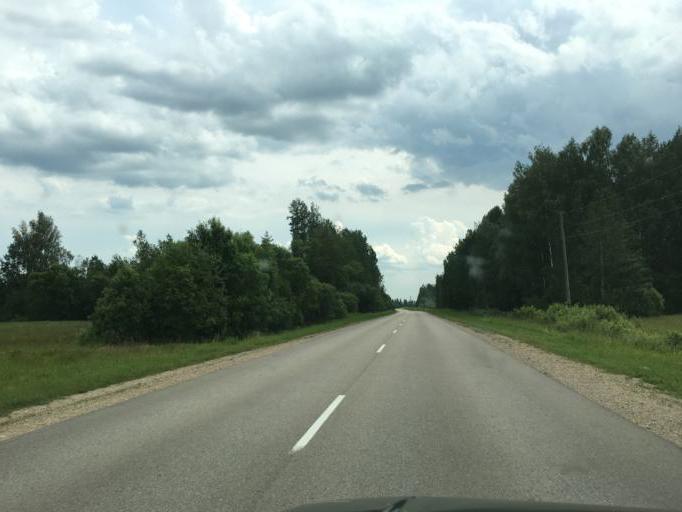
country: LV
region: Rugaju
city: Rugaji
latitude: 56.9534
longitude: 27.0676
